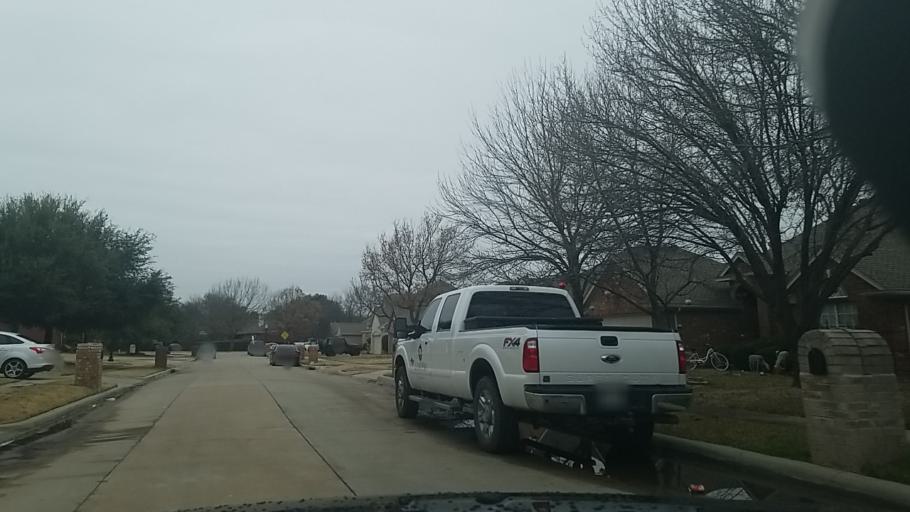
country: US
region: Texas
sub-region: Denton County
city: Corinth
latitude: 33.1560
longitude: -97.0687
